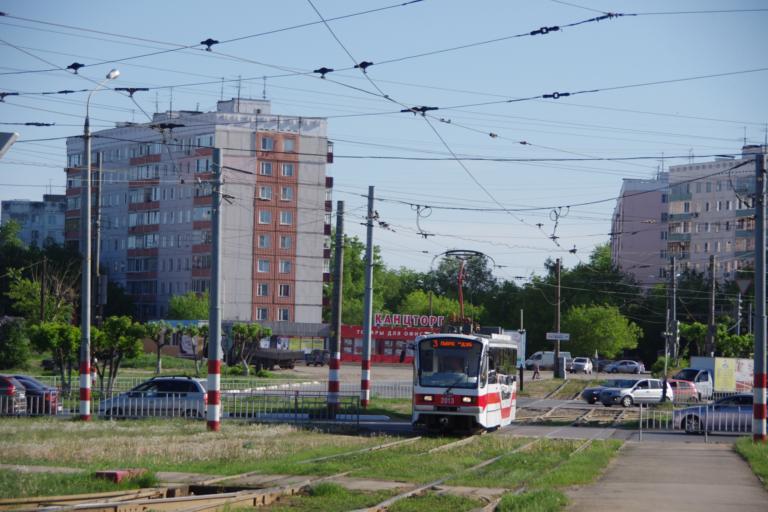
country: RU
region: Nizjnij Novgorod
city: Nizhniy Novgorod
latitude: 56.2988
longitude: 43.9445
